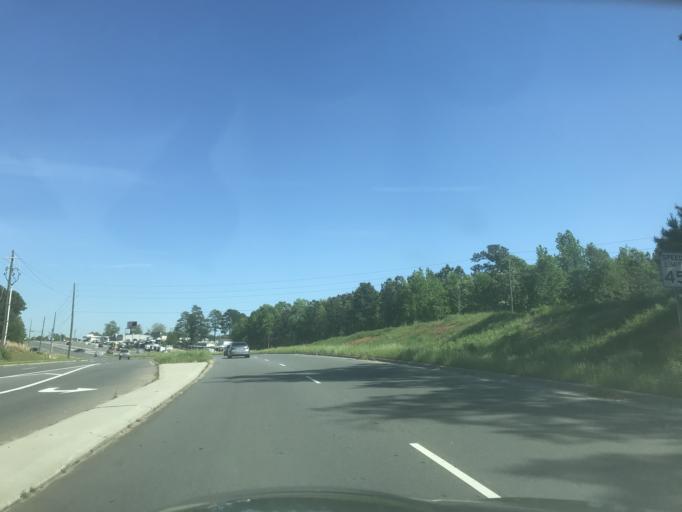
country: US
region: North Carolina
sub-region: Wake County
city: Raleigh
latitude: 35.7318
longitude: -78.6566
